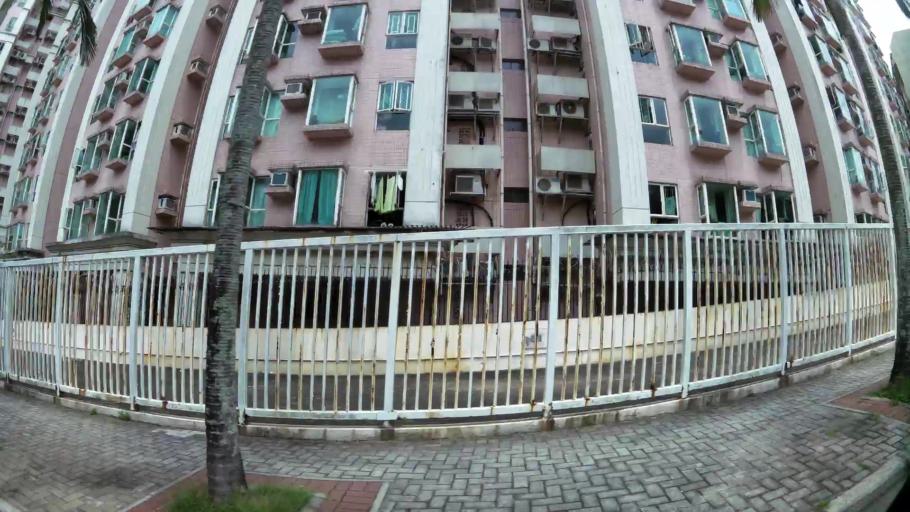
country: HK
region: Wanchai
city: Wan Chai
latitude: 22.2874
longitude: 114.2041
